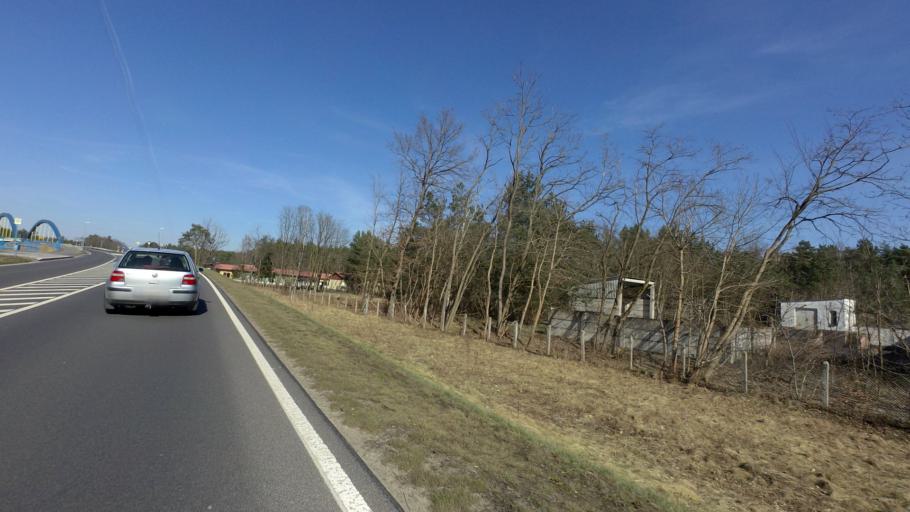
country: DE
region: Brandenburg
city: Eberswalde
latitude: 52.8546
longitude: 13.8281
